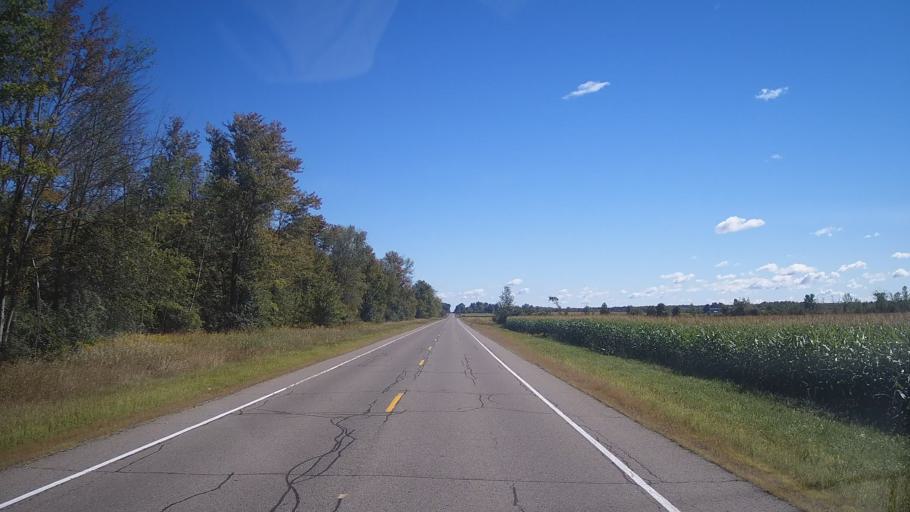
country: US
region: New York
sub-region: St. Lawrence County
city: Ogdensburg
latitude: 44.9318
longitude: -75.3282
